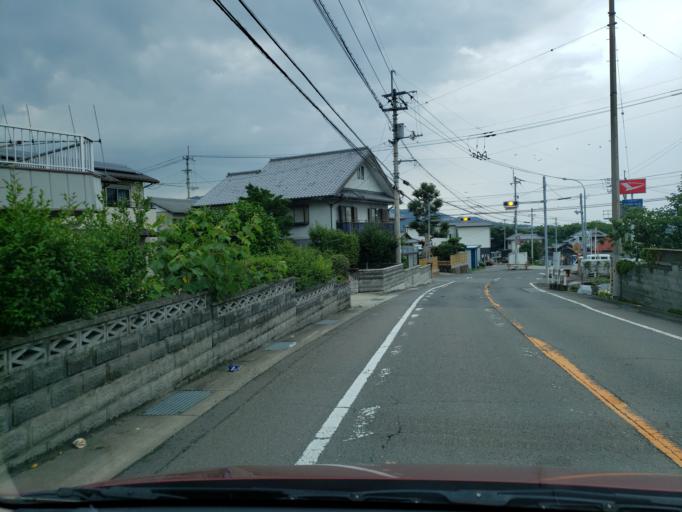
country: JP
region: Tokushima
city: Kamojimacho-jogejima
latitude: 34.1048
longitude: 134.2643
